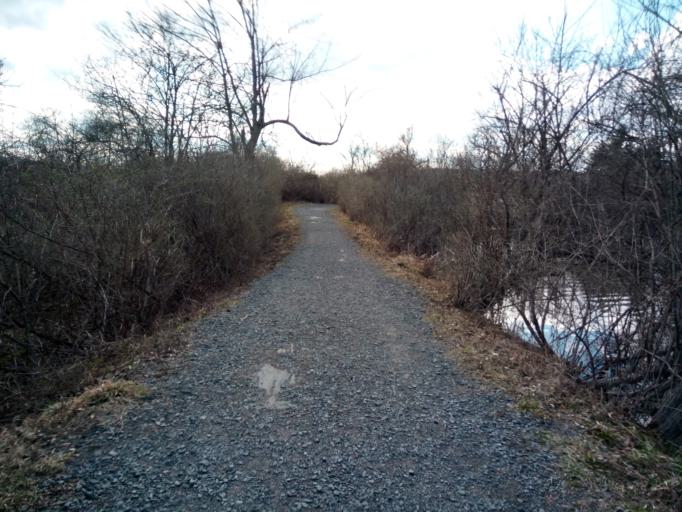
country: US
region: New York
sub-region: Chemung County
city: Big Flats
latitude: 42.1462
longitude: -76.9133
